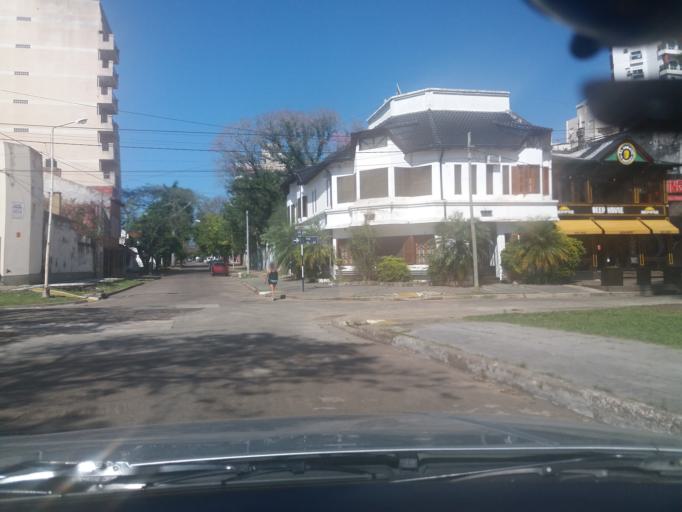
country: AR
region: Corrientes
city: Corrientes
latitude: -27.4664
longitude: -58.8493
